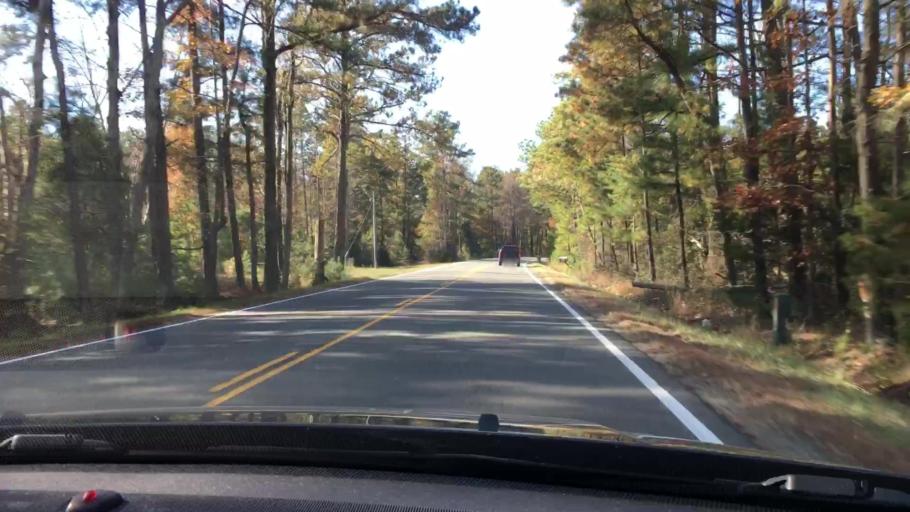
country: US
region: Virginia
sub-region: Hanover County
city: Hanover
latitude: 37.8316
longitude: -77.3598
